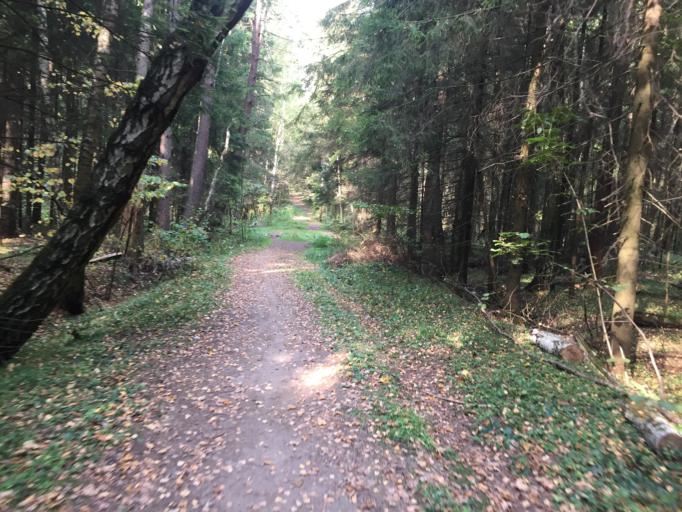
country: RU
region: Moscow
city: Babushkin
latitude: 55.8583
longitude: 37.7435
